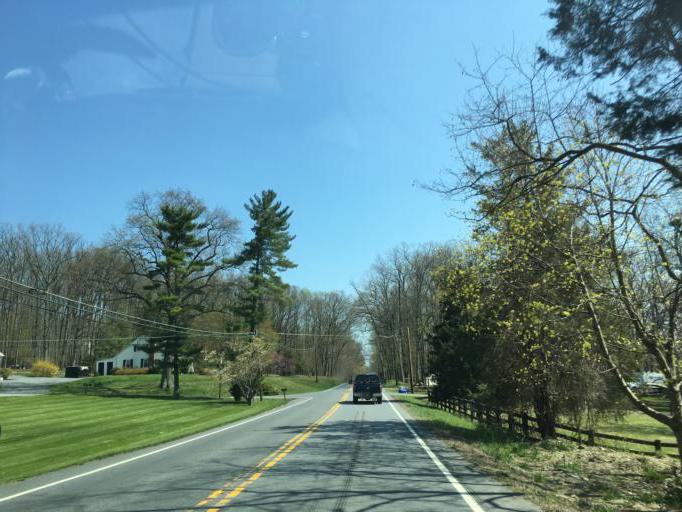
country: US
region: Maryland
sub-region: Frederick County
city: Woodsboro
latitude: 39.5055
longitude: -77.2723
